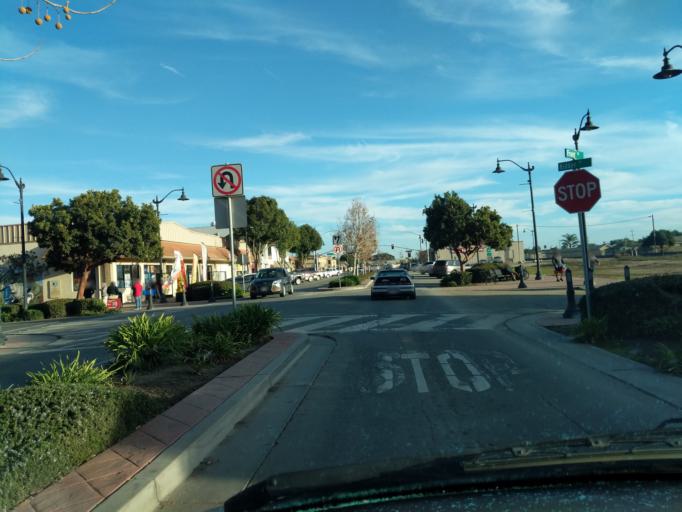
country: US
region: California
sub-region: Monterey County
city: Soledad
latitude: 36.4257
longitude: -121.3274
